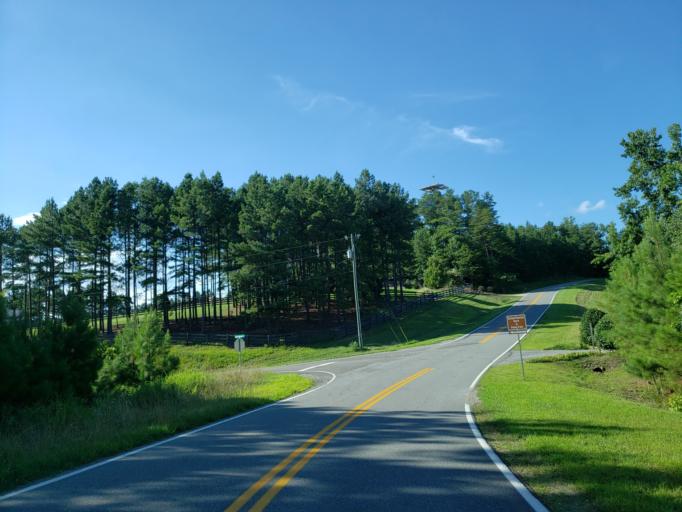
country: US
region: Georgia
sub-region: Bartow County
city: Rydal
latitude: 34.3578
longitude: -84.6108
